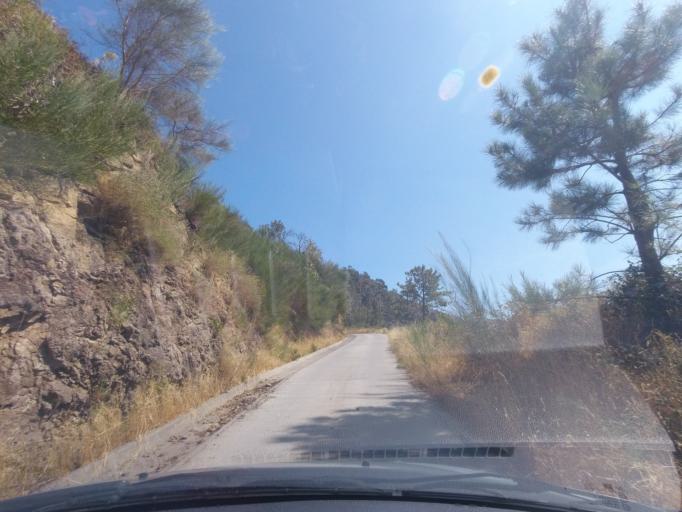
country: PT
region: Madeira
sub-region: Sao Vicente
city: Sao Vicente
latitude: 32.7425
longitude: -17.0295
